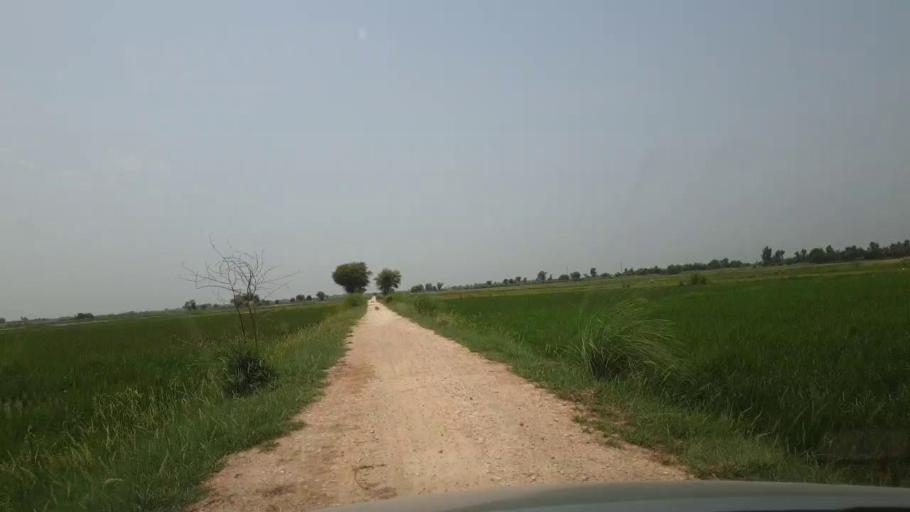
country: PK
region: Sindh
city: Garhi Yasin
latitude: 27.8663
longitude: 68.4855
